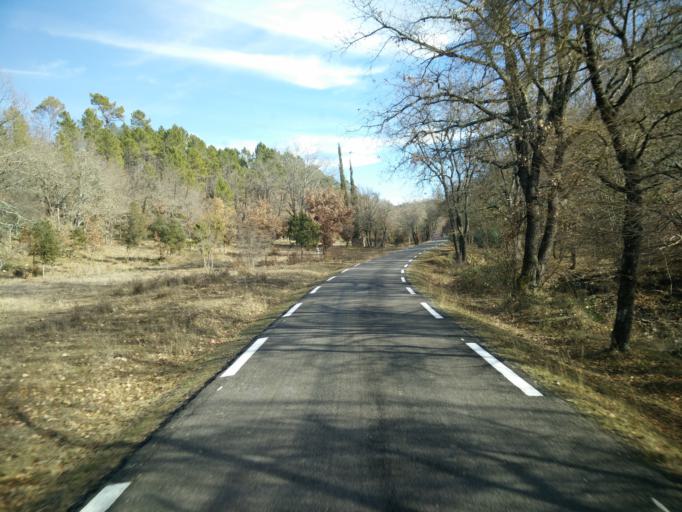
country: FR
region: Provence-Alpes-Cote d'Azur
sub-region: Departement du Var
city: Saint-Paul-en-Foret
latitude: 43.5712
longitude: 6.6677
